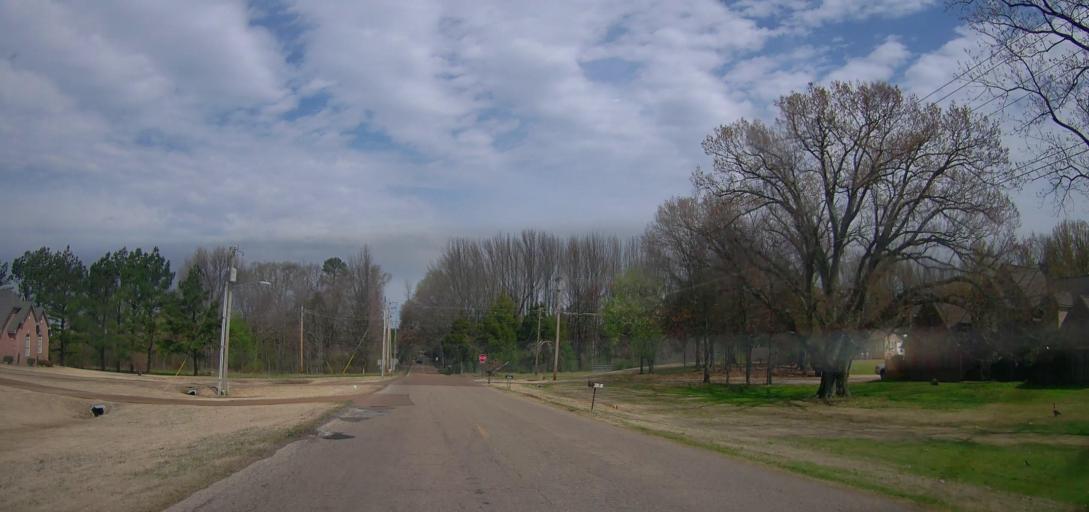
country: US
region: Mississippi
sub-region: De Soto County
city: Olive Branch
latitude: 34.9937
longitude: -89.8484
